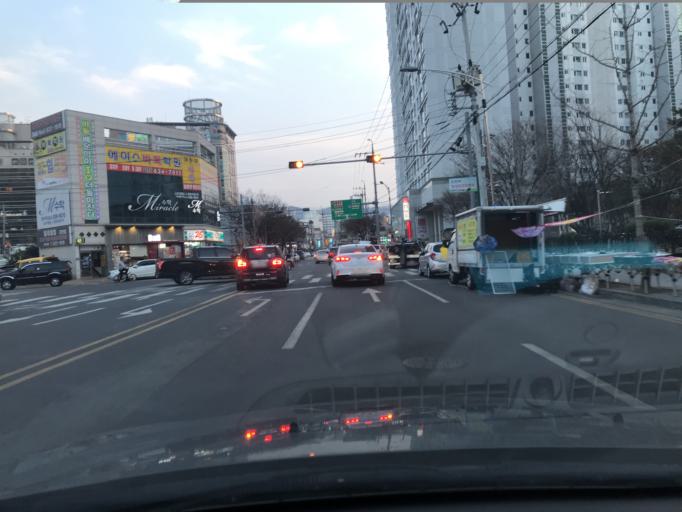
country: KR
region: Daegu
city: Hwawon
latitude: 35.8148
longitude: 128.5206
